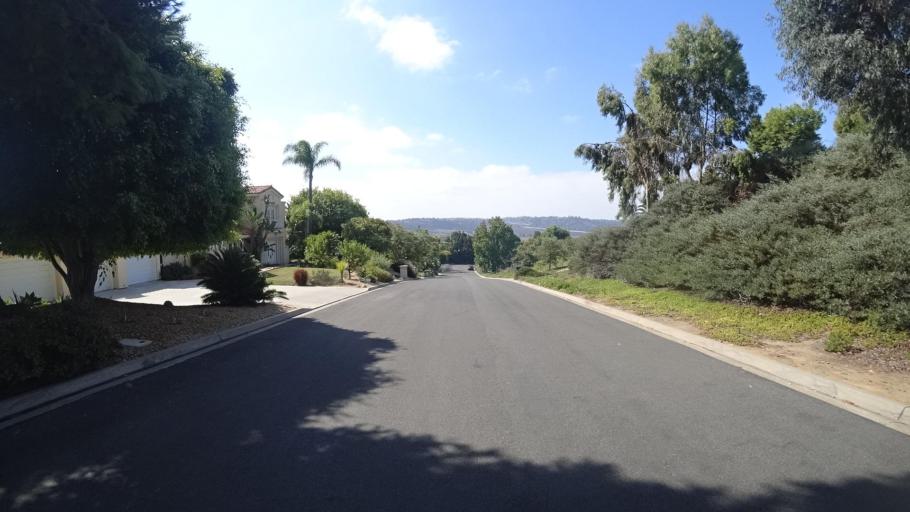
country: US
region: California
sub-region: San Diego County
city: Solana Beach
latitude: 32.9840
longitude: -117.2355
